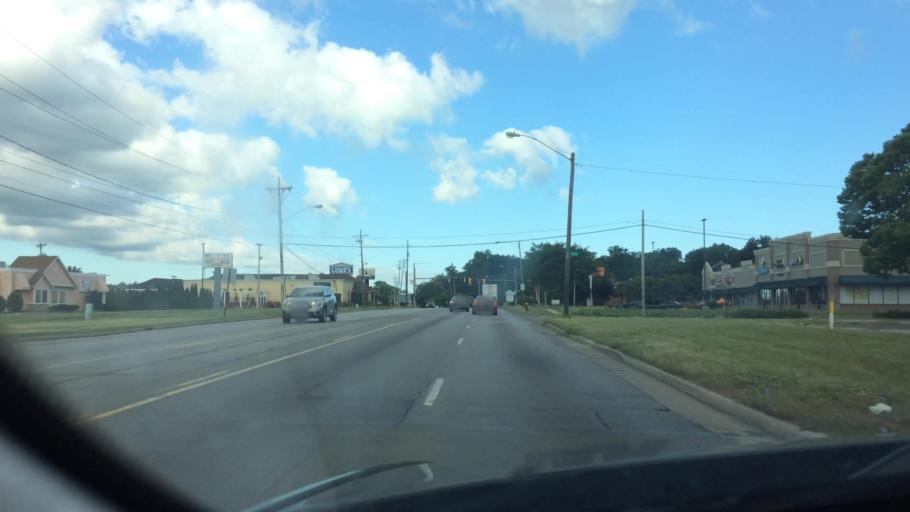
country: US
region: Ohio
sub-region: Lucas County
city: Holland
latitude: 41.6167
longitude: -83.6673
